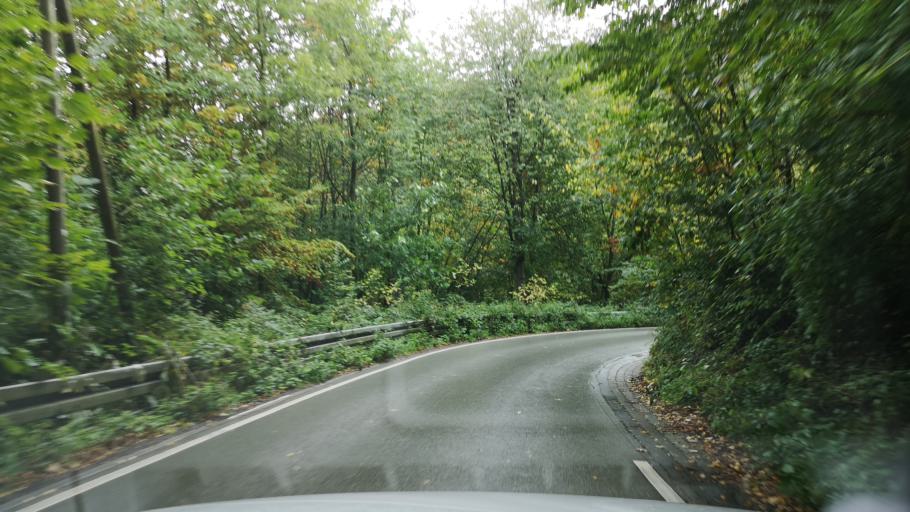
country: DE
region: North Rhine-Westphalia
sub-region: Regierungsbezirk Dusseldorf
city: Heiligenhaus
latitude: 51.3732
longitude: 6.9963
